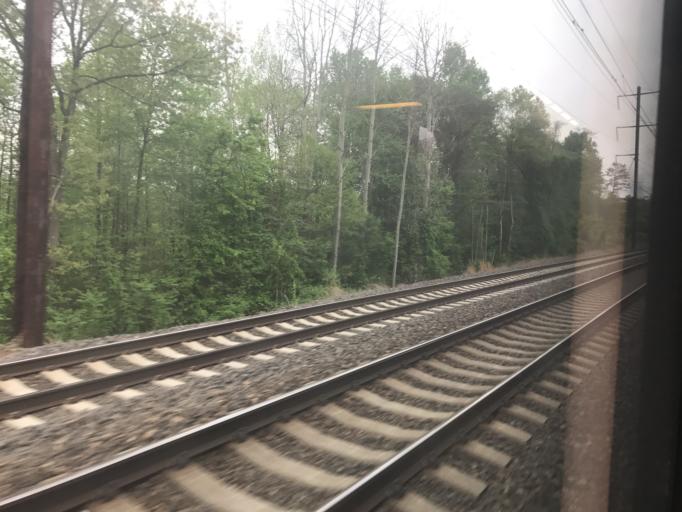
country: US
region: Maryland
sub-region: Prince George's County
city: Glenn Dale
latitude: 39.0219
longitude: -76.7612
